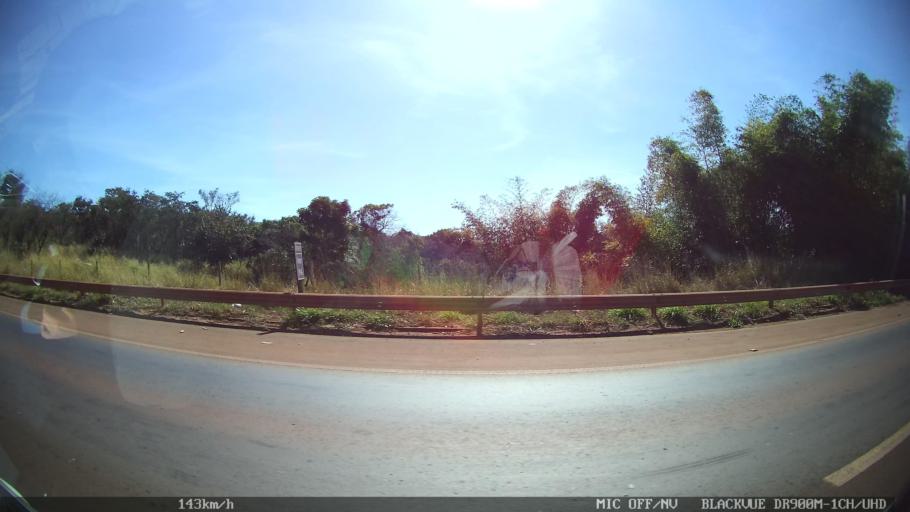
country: BR
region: Sao Paulo
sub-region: Barretos
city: Barretos
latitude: -20.5222
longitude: -48.5811
